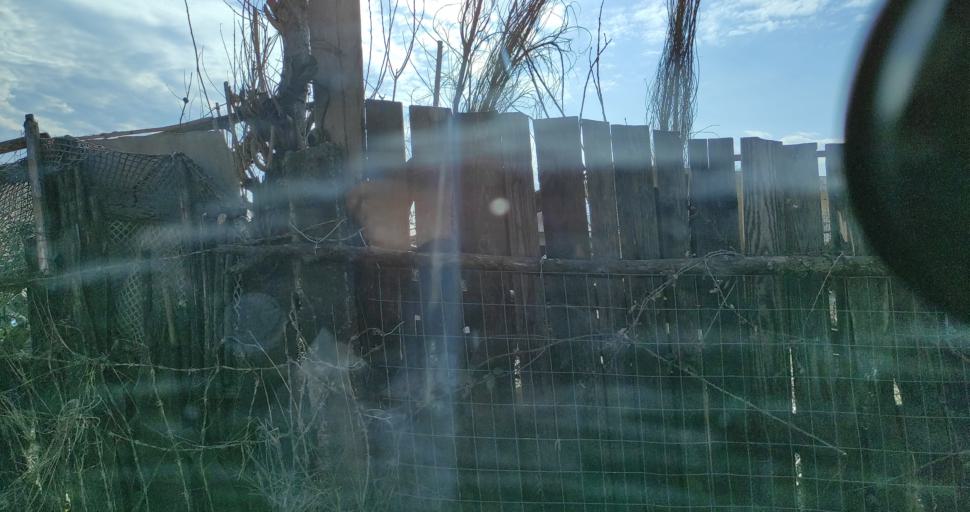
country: AL
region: Lezhe
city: Lezhe
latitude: 41.7810
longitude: 19.6314
